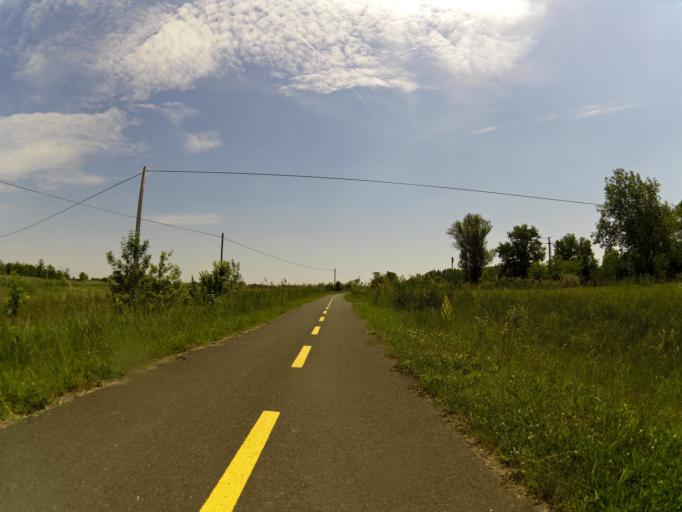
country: HU
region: Csongrad
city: Balastya
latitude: 46.4353
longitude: 20.0079
